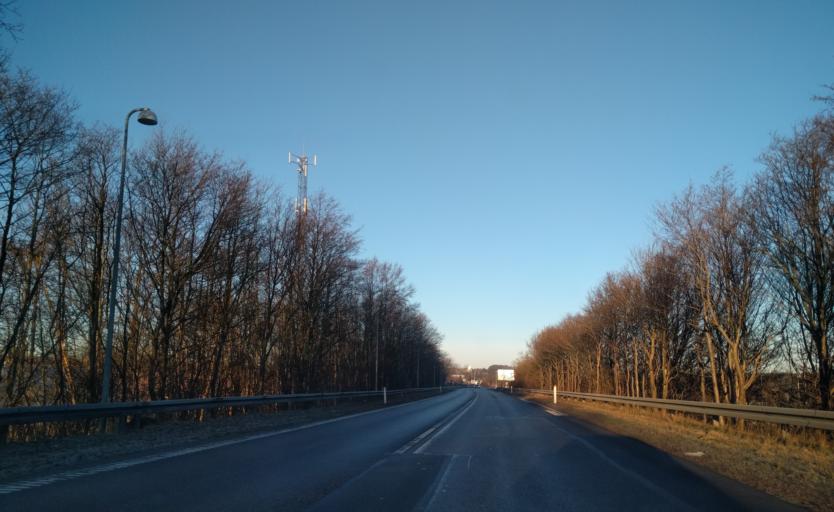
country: DK
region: North Denmark
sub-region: Alborg Kommune
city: Vestbjerg
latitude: 57.0869
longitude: 9.9632
